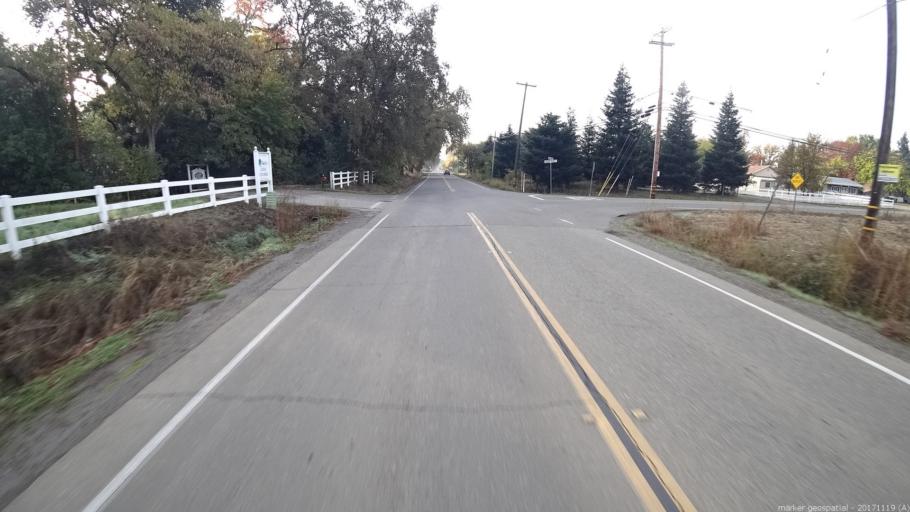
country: US
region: California
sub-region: Shasta County
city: Anderson
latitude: 40.5059
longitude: -122.3242
